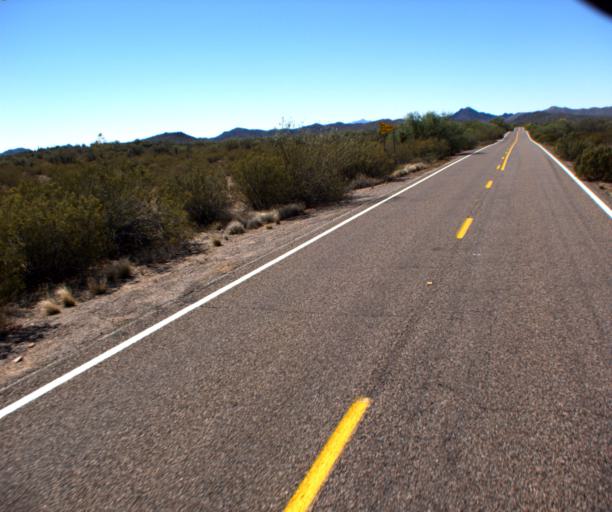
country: MX
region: Sonora
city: Sonoyta
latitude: 32.0374
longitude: -112.7965
